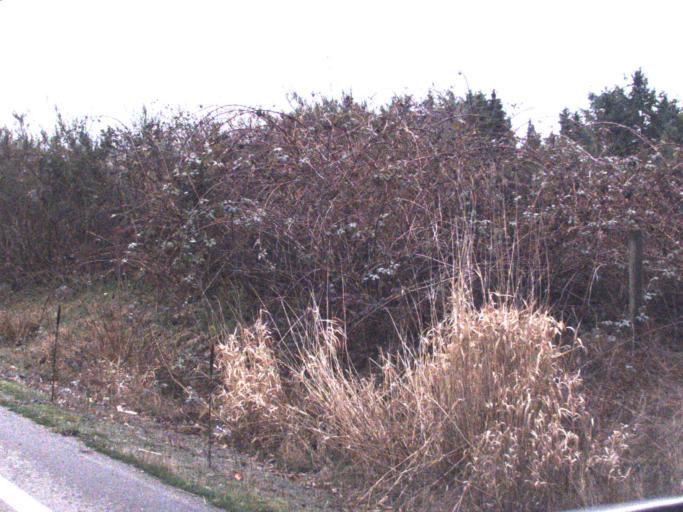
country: US
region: Washington
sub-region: Snohomish County
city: Sisco Heights
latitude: 48.1516
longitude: -122.1199
